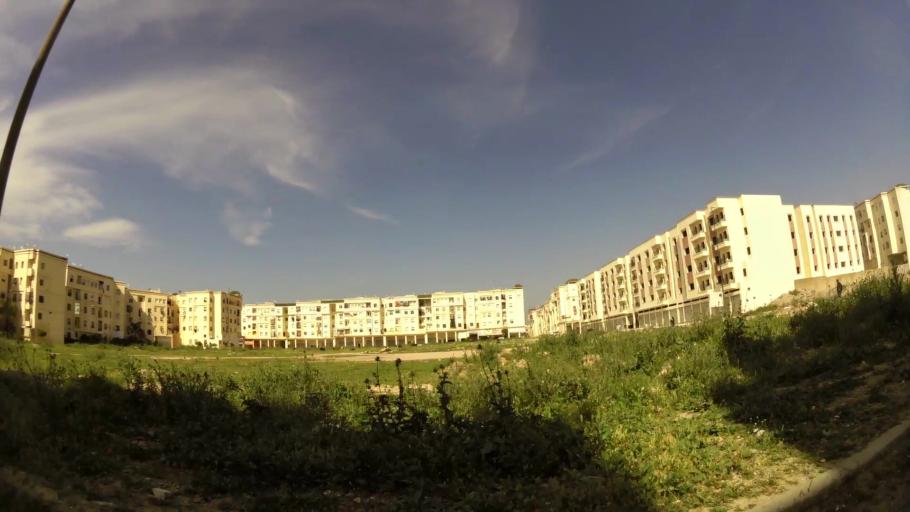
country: MA
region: Fes-Boulemane
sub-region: Fes
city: Fes
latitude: 34.0128
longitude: -5.0423
